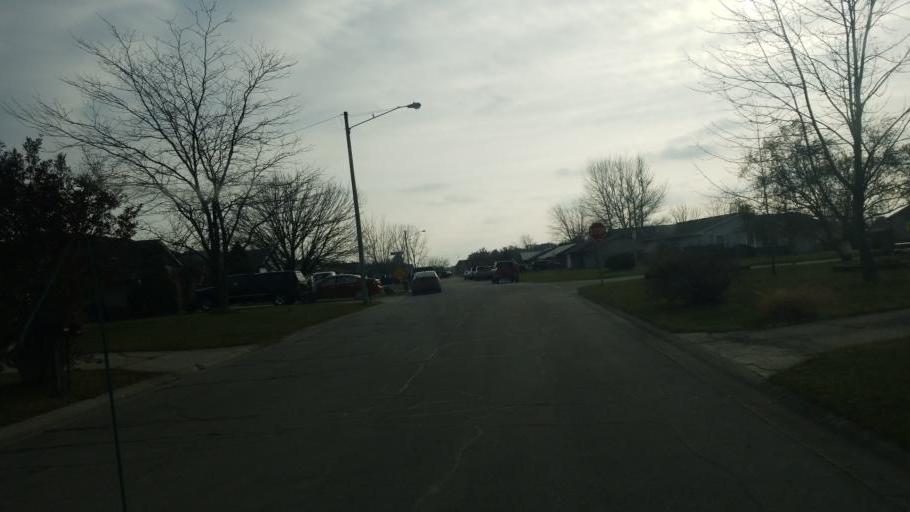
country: US
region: Indiana
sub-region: Adams County
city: Berne
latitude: 40.6464
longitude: -84.9510
